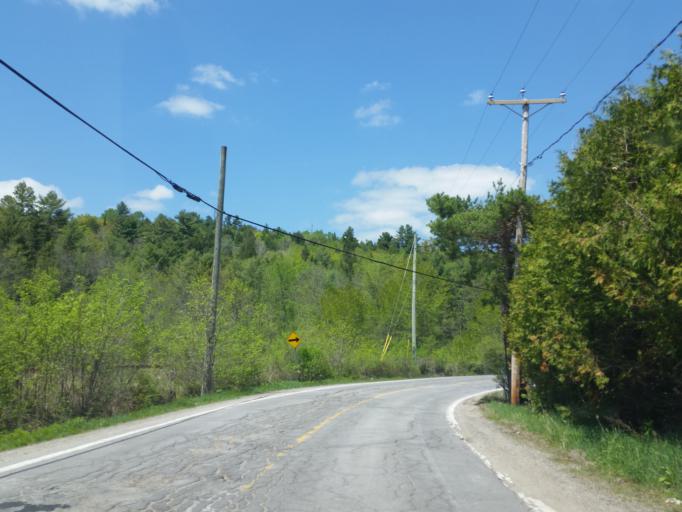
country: CA
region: Quebec
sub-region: Outaouais
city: Wakefield
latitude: 45.6093
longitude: -75.8974
